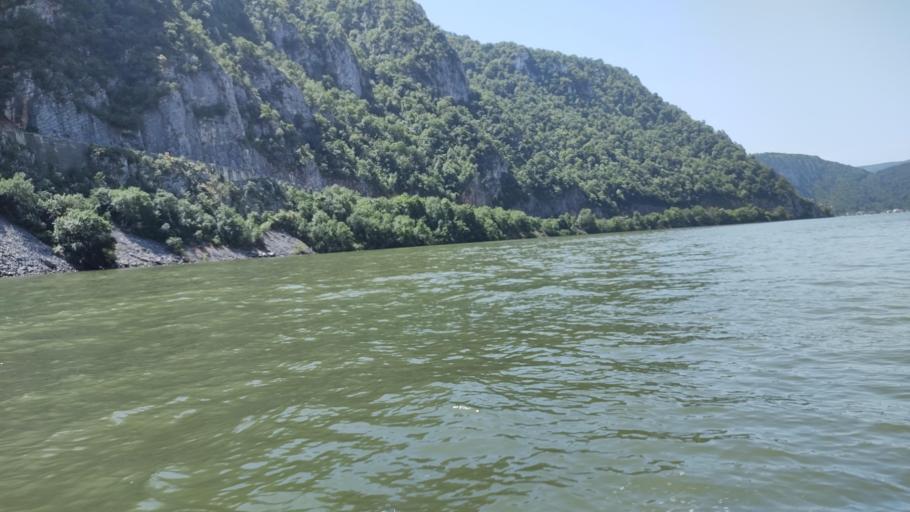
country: RO
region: Mehedinti
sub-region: Comuna Dubova
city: Dubova
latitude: 44.6328
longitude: 22.2888
